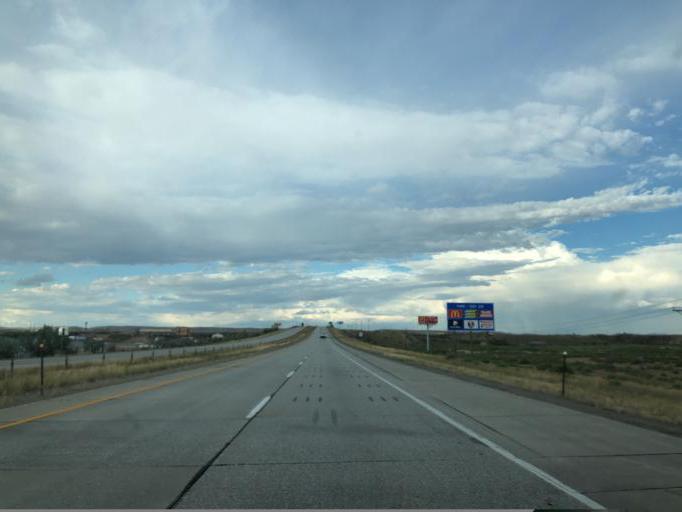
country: US
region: Wyoming
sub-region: Carbon County
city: Rawlins
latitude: 41.7827
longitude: -107.2129
